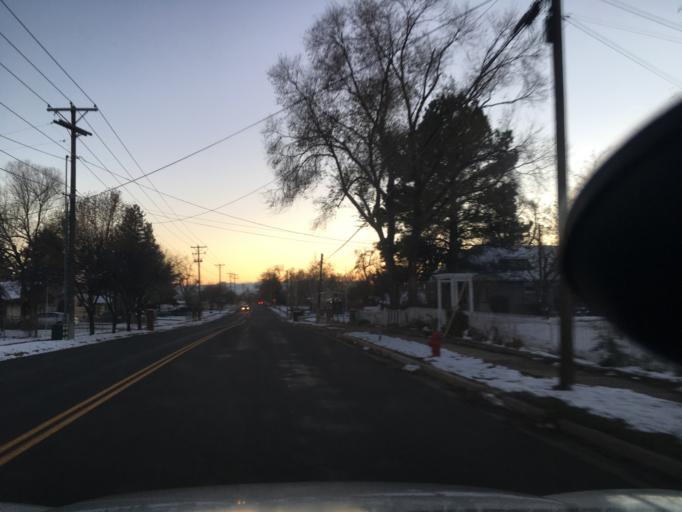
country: US
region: Utah
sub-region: Davis County
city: Layton
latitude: 41.0656
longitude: -111.9658
